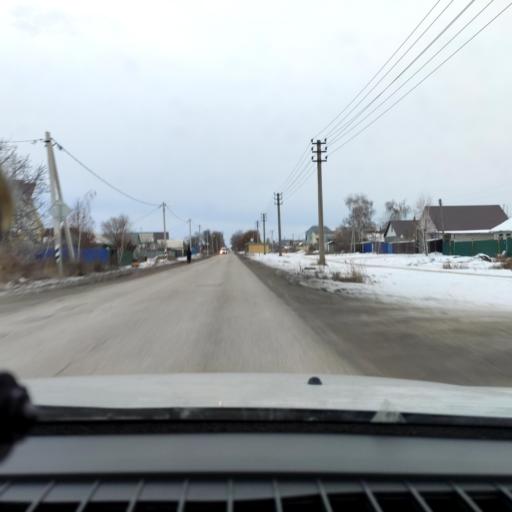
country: RU
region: Samara
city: Chapayevsk
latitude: 52.9975
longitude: 49.7164
